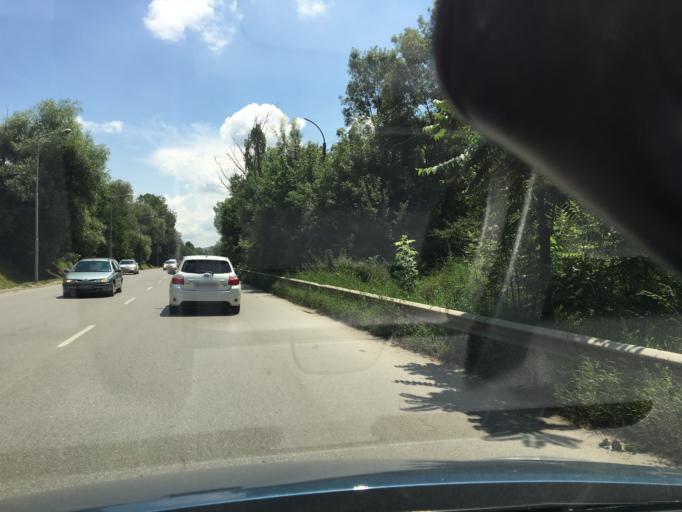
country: BG
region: Sofia-Capital
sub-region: Stolichna Obshtina
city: Sofia
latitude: 42.6622
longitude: 23.3039
